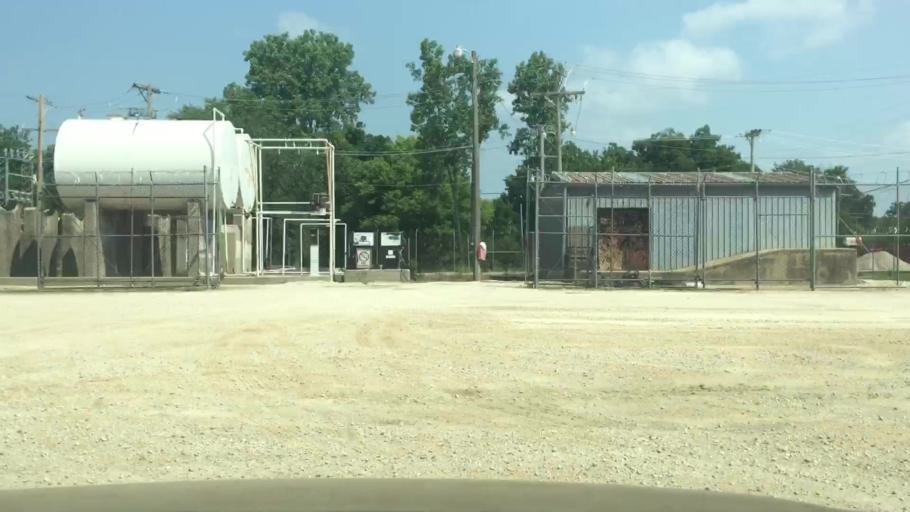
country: US
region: Kansas
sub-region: Allen County
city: Iola
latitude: 37.9086
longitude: -95.4060
